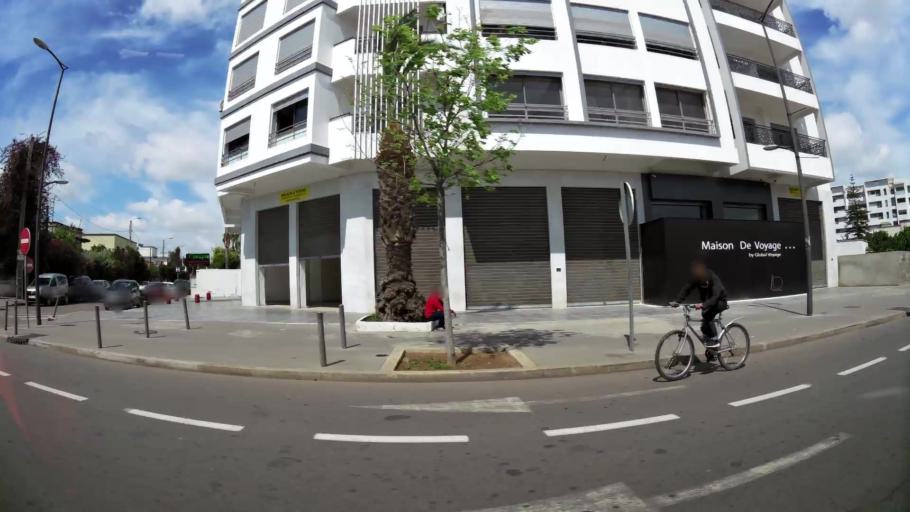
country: MA
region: Grand Casablanca
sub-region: Casablanca
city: Casablanca
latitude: 33.5653
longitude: -7.6270
